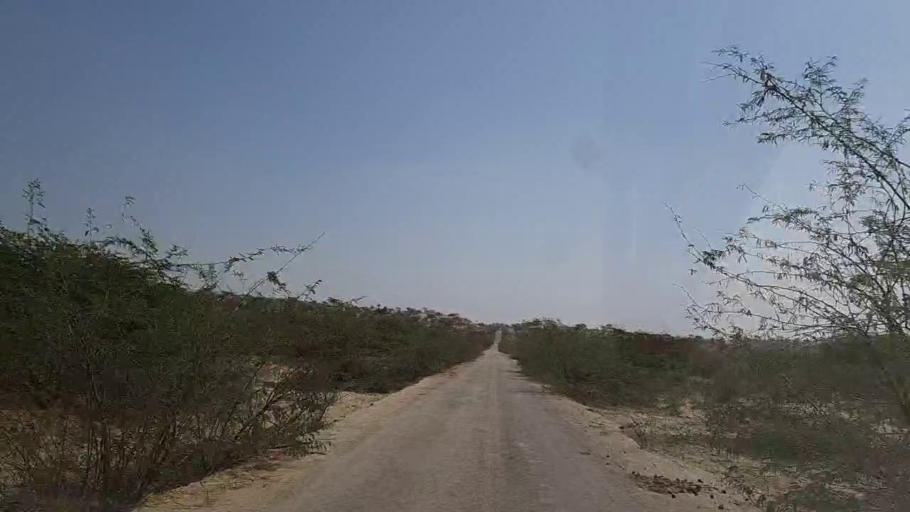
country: PK
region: Sindh
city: Diplo
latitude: 24.4931
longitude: 69.4351
